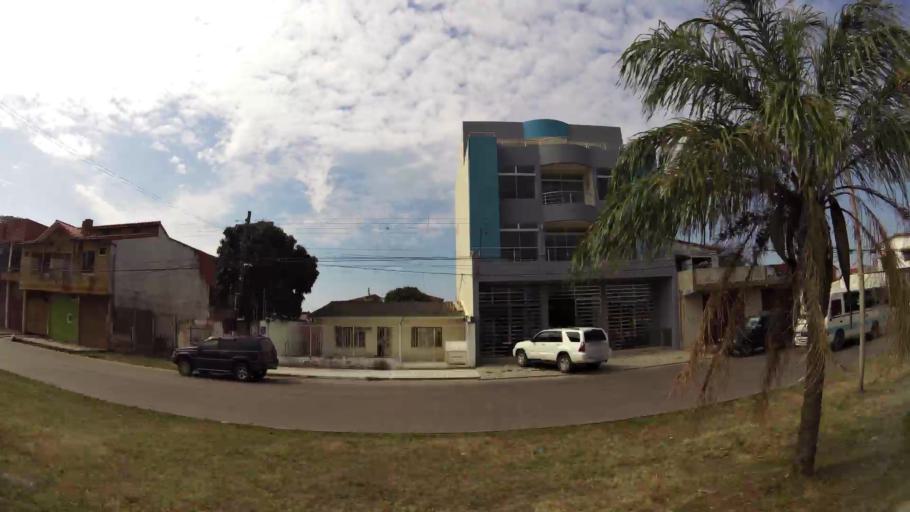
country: BO
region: Santa Cruz
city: Santa Cruz de la Sierra
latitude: -17.7498
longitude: -63.1540
